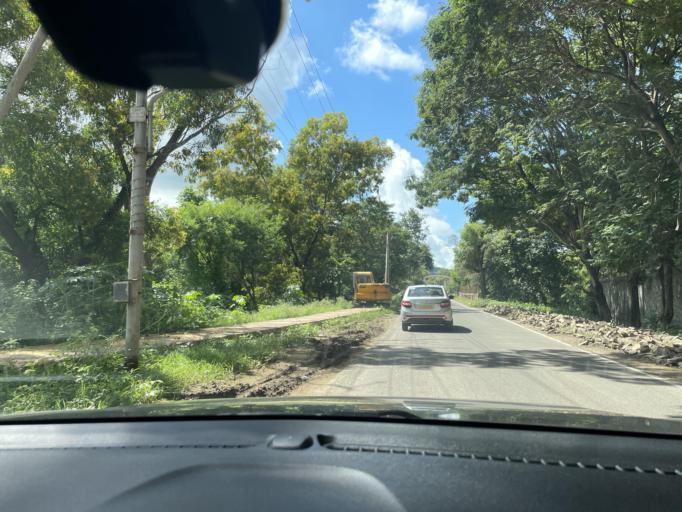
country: IN
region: Maharashtra
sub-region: Pune Division
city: Shivaji Nagar
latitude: 18.5271
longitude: 73.7794
